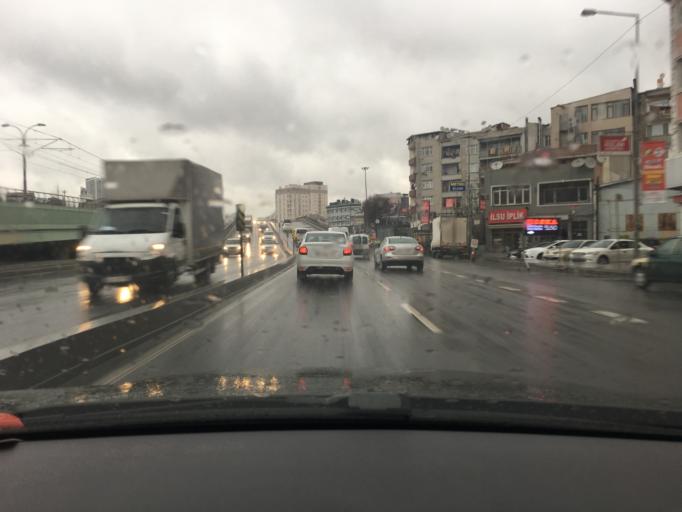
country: TR
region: Istanbul
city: merter keresteciler
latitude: 41.0325
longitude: 28.8971
